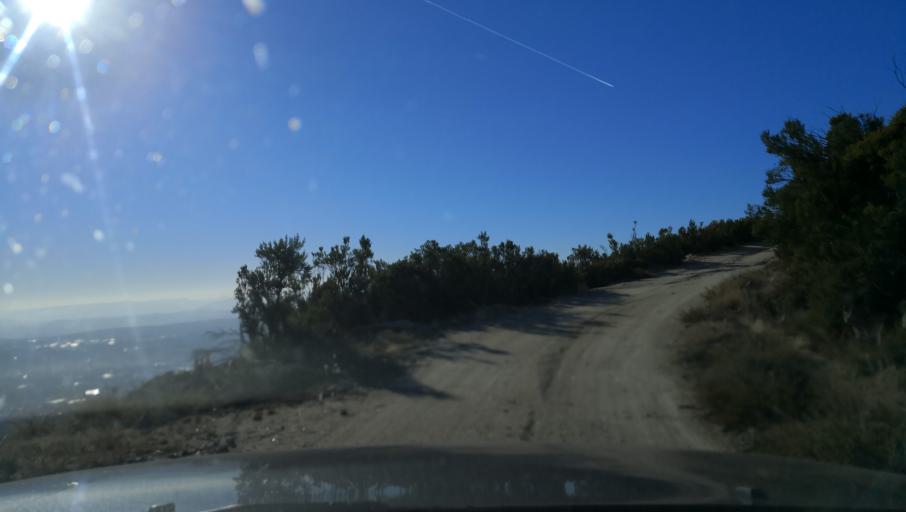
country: PT
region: Vila Real
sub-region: Vila Real
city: Vila Real
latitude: 41.3497
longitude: -7.7644
